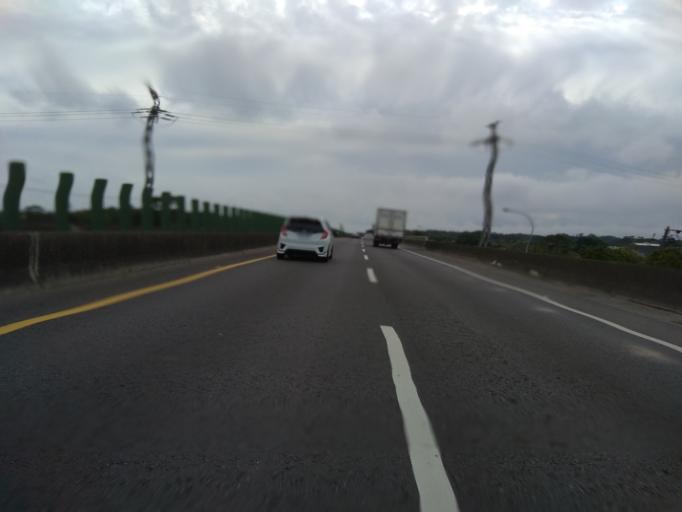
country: TW
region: Taiwan
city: Daxi
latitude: 24.9416
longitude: 121.1769
